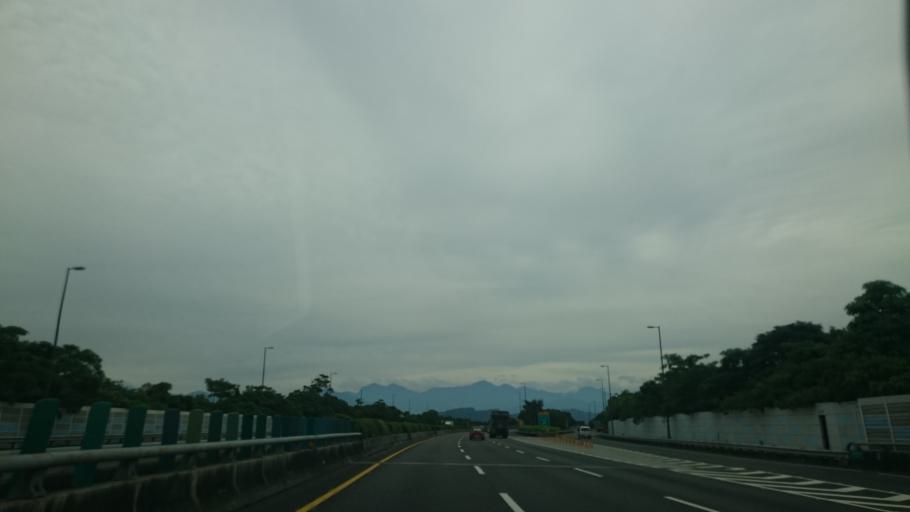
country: TW
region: Taiwan
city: Zhongxing New Village
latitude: 23.9532
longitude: 120.6651
